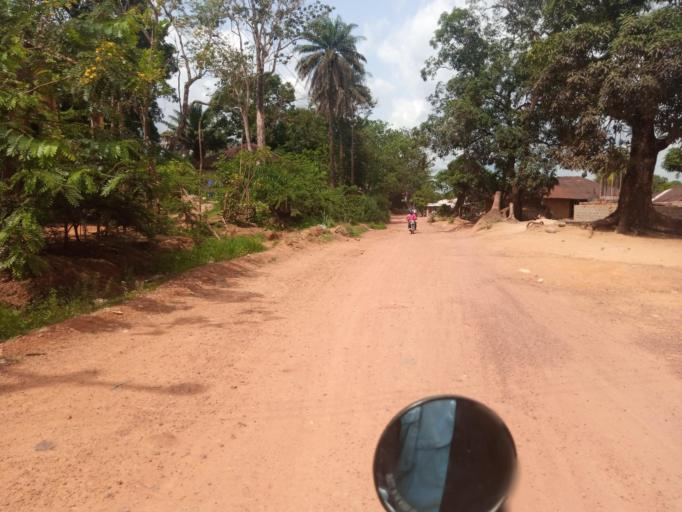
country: SL
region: Southern Province
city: Bo
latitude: 7.9759
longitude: -11.7386
